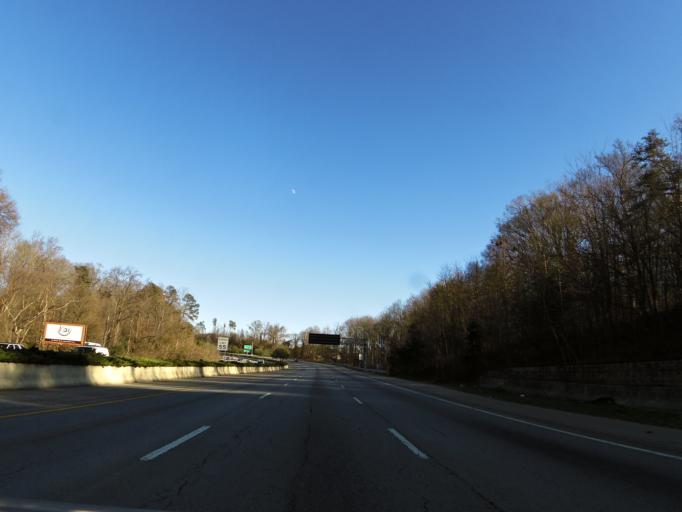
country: US
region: South Carolina
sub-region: Greenville County
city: Greenville
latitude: 34.8519
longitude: -82.3719
